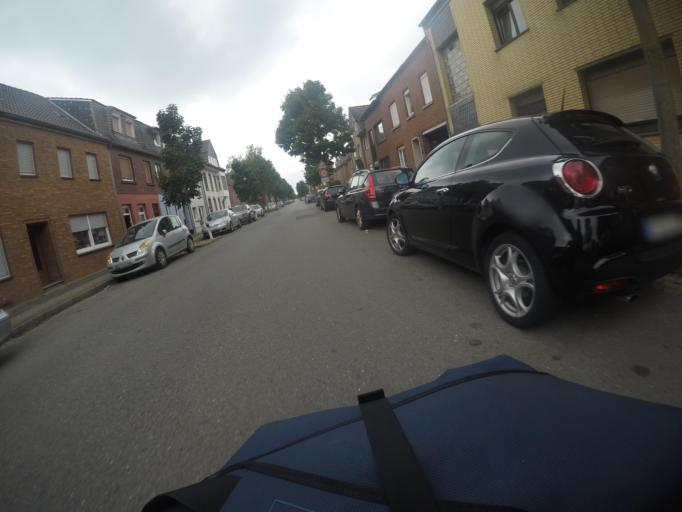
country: DE
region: North Rhine-Westphalia
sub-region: Regierungsbezirk Dusseldorf
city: Kevelaer
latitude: 51.5870
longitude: 6.2415
